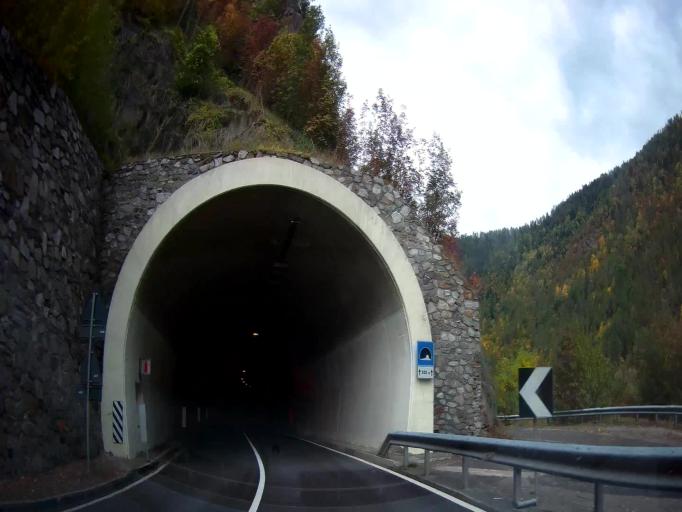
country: IT
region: Trentino-Alto Adige
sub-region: Bolzano
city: Naturno
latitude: 46.6612
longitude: 10.9543
